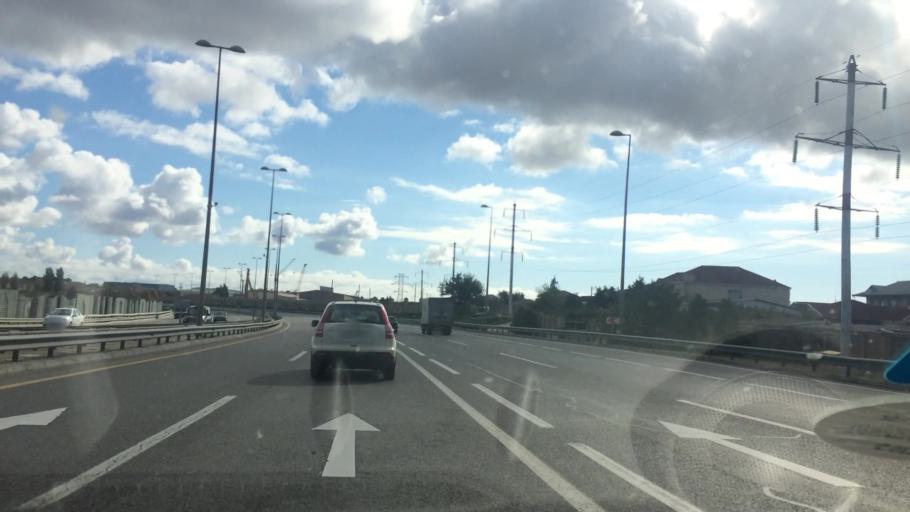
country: AZ
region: Baki
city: Ramana
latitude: 40.4389
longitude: 49.9747
